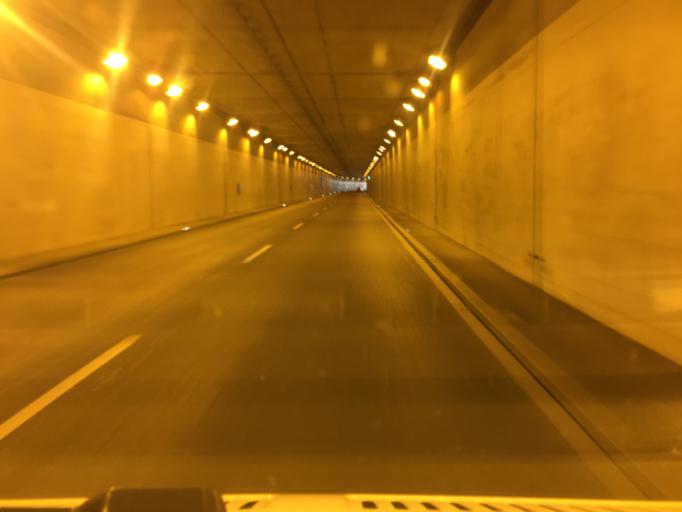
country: DE
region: Saxony
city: Zwickau
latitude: 50.7205
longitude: 12.5021
